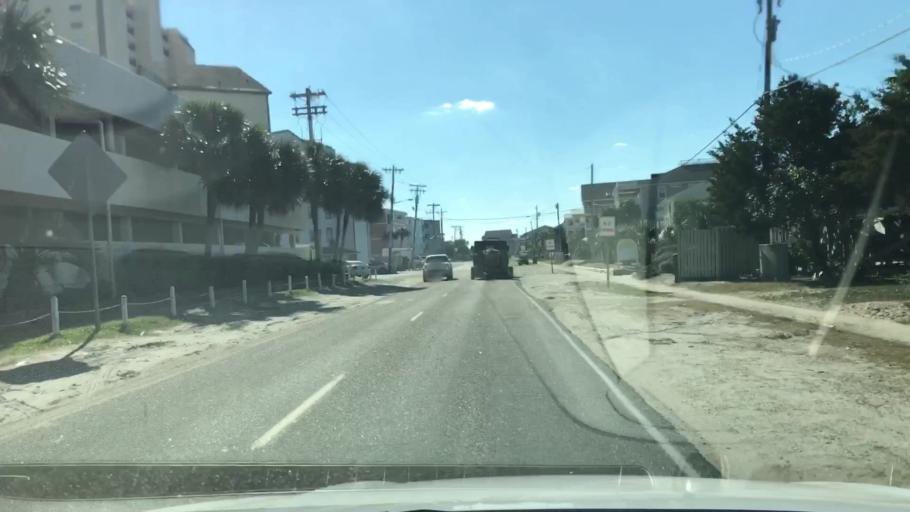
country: US
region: South Carolina
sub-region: Horry County
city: Garden City
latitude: 33.5846
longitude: -78.9919
